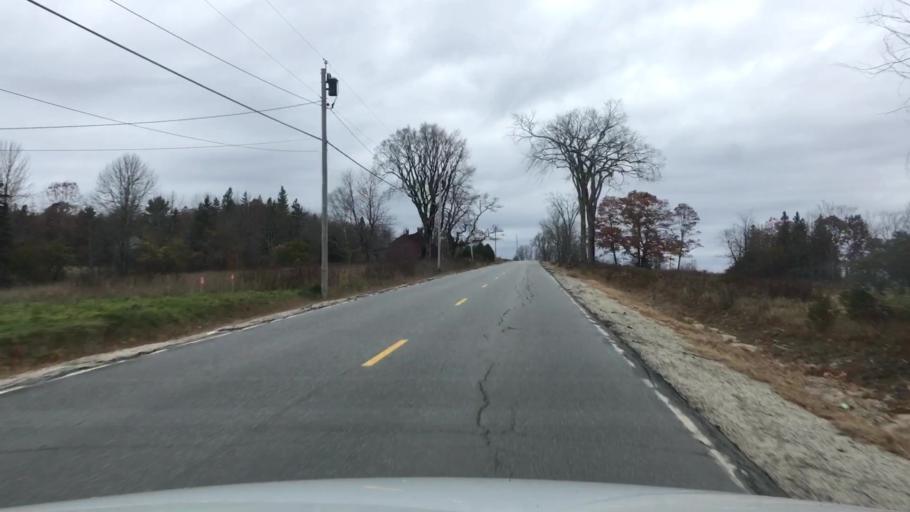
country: US
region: Maine
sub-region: Hancock County
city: Penobscot
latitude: 44.4382
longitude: -68.6337
